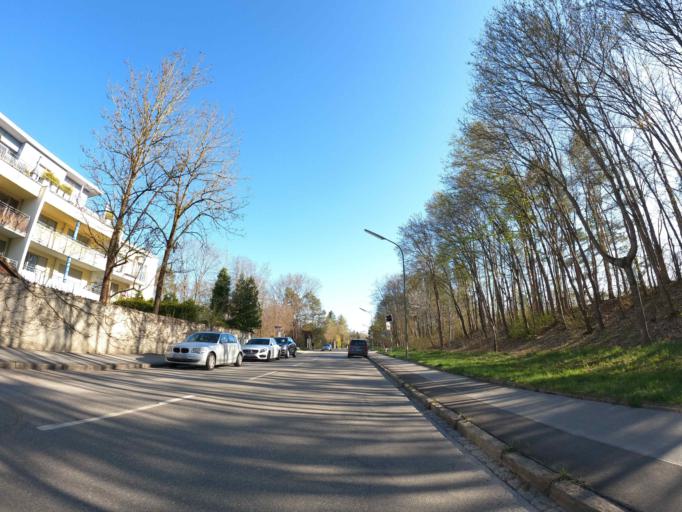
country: DE
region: Bavaria
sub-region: Upper Bavaria
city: Ottobrunn
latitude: 48.0670
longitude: 11.6533
